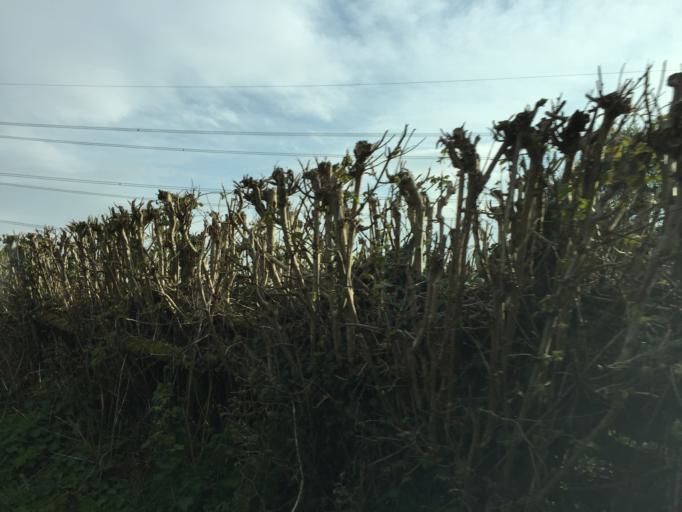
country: GB
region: Wales
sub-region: Caerphilly County Borough
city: Maesycwmmer
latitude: 51.6271
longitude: -3.2194
